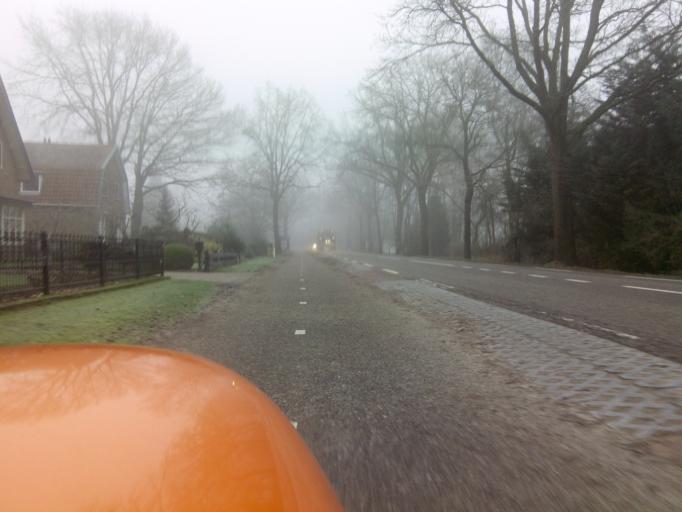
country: NL
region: Utrecht
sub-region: Gemeente Leusden
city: Leusden
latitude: 52.1521
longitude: 5.4362
